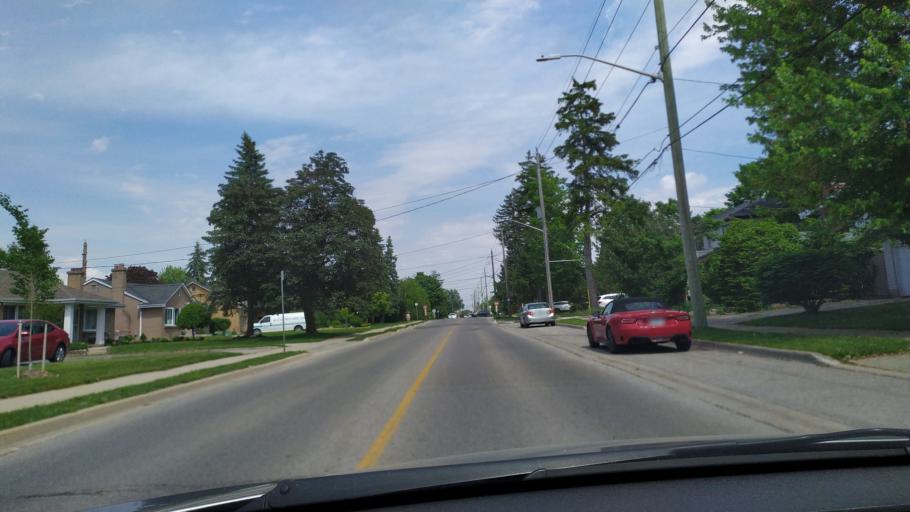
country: CA
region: Ontario
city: London
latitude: 42.9612
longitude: -81.2378
